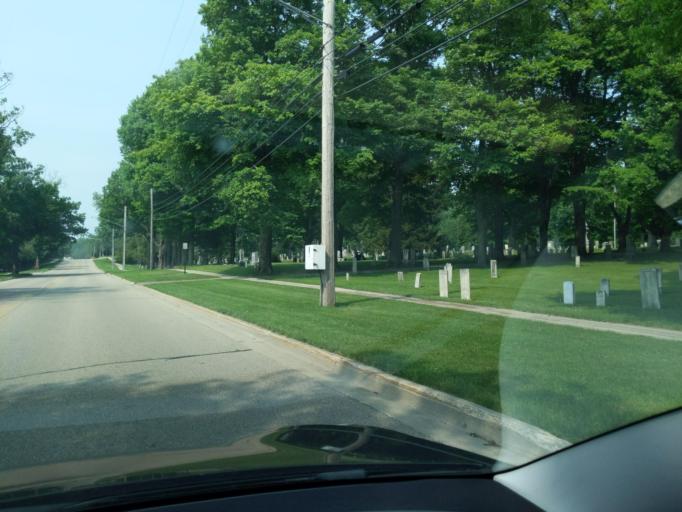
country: US
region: Michigan
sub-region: Clinton County
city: DeWitt
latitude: 42.8475
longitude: -84.5690
